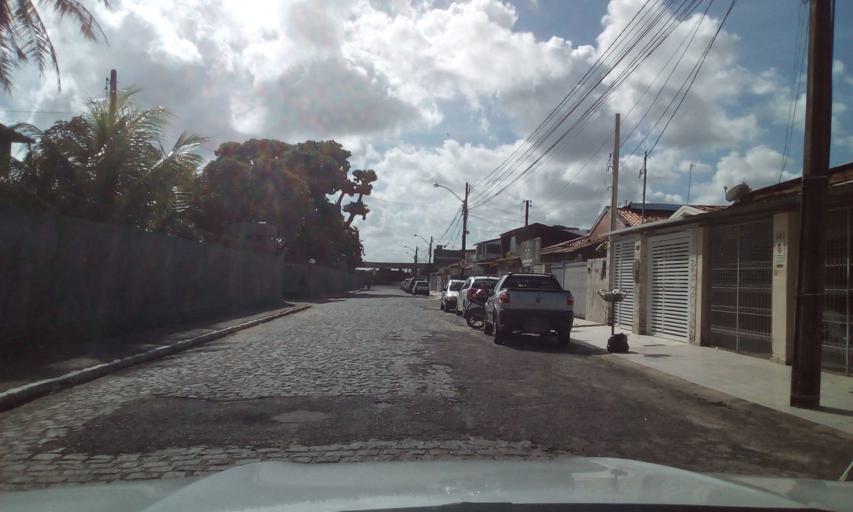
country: BR
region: Paraiba
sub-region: Joao Pessoa
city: Joao Pessoa
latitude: -7.1371
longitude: -34.8838
